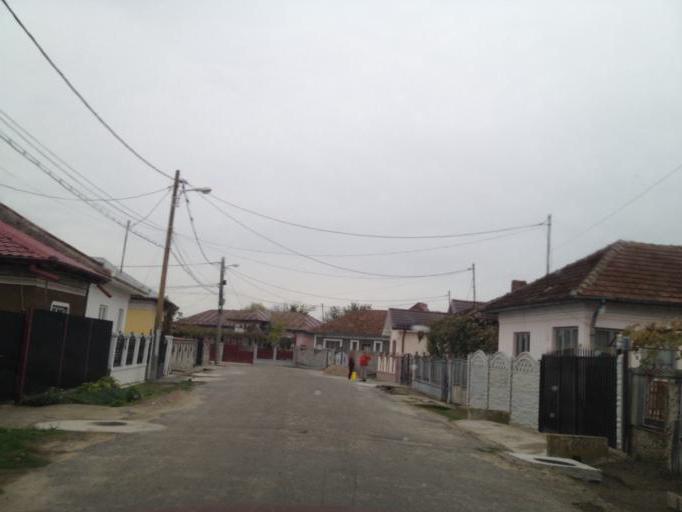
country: RO
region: Dolj
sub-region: Municipiul Craiova
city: Mofleni
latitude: 44.2987
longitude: 23.7599
